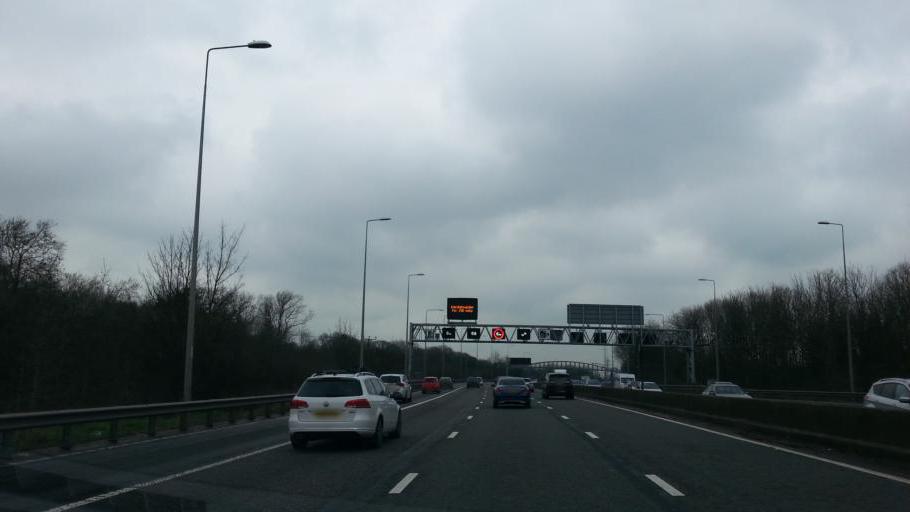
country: GB
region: England
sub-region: South Gloucestershire
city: Almondsbury
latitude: 51.5376
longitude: -2.5890
